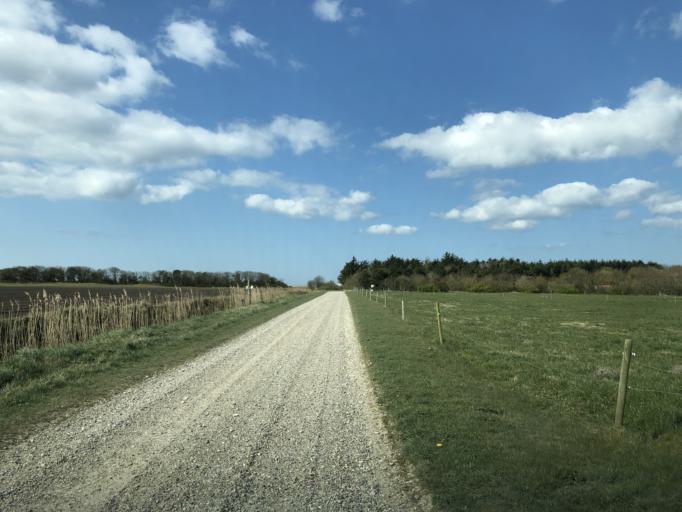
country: DK
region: Central Jutland
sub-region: Lemvig Kommune
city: Lemvig
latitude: 56.4032
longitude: 8.1755
